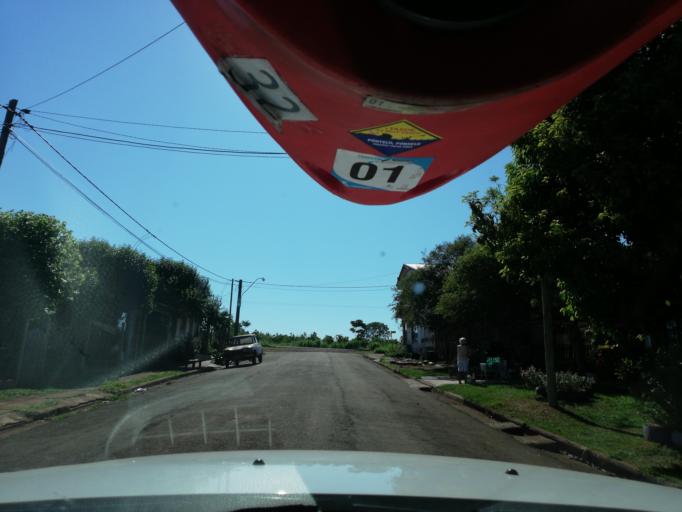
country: AR
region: Misiones
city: Puerto Leoni
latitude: -26.9896
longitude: -55.1653
